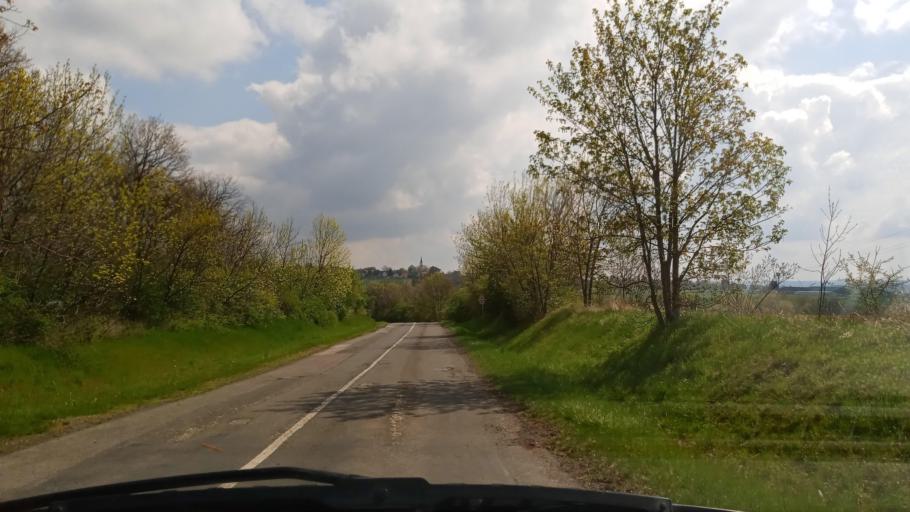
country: HU
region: Baranya
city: Pecsvarad
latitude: 46.1089
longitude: 18.5064
